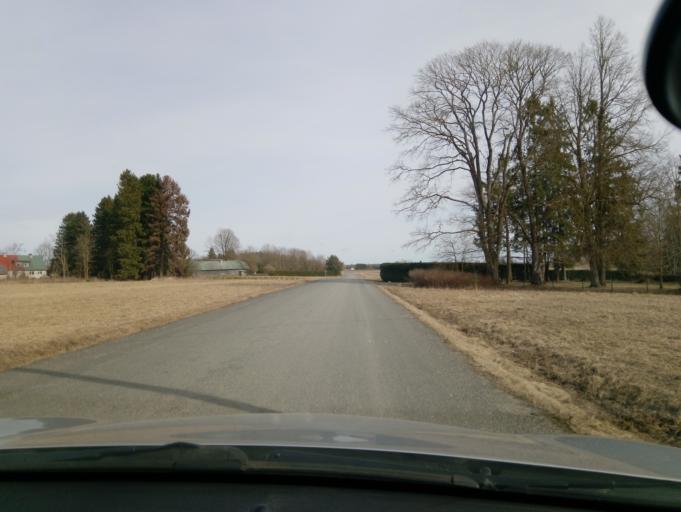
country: EE
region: Jaervamaa
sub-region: Tueri vald
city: Tueri
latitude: 58.8583
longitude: 25.4228
